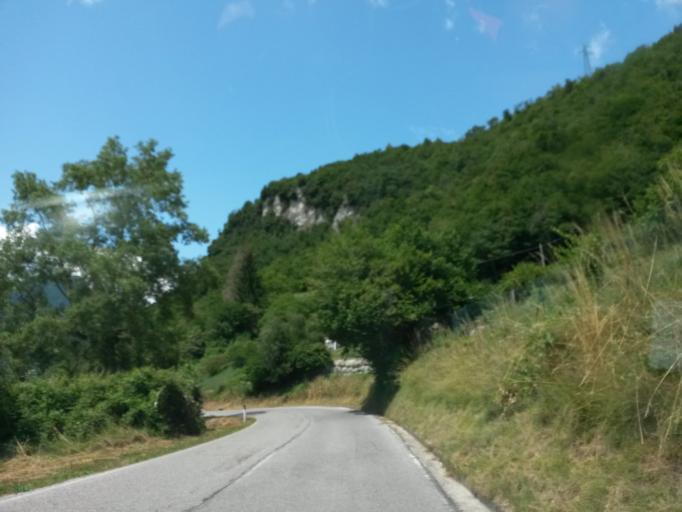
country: IT
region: Lombardy
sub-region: Provincia di Brescia
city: Gargnano
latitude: 45.6839
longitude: 10.6236
